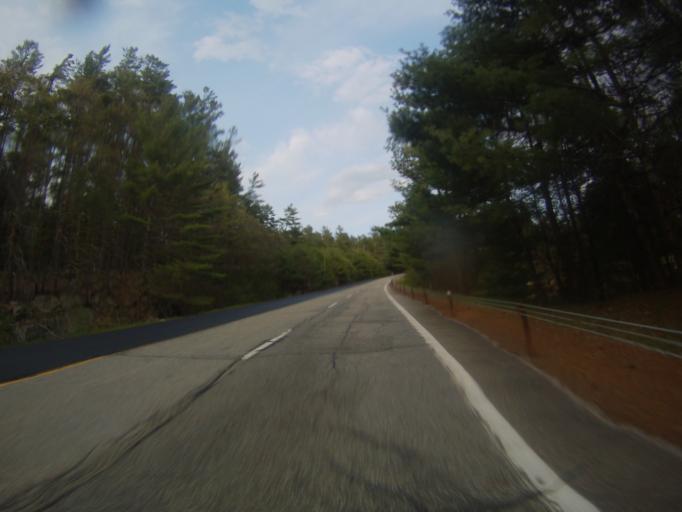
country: US
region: New York
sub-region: Essex County
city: Ticonderoga
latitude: 43.7441
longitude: -73.6350
